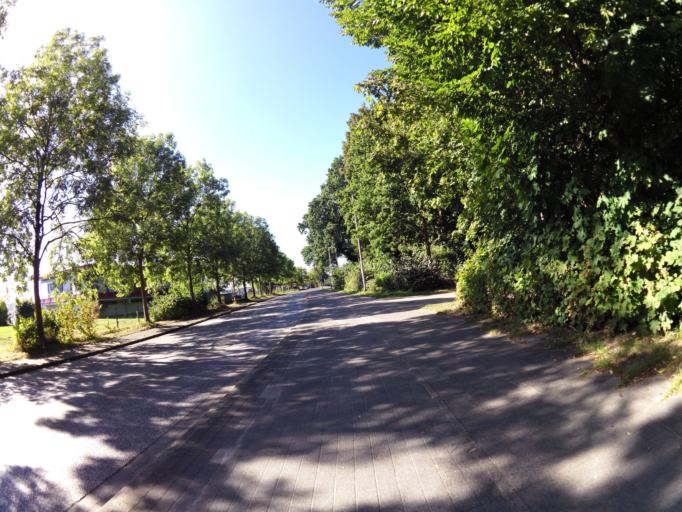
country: DE
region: Schleswig-Holstein
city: Eckernforde
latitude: 54.4772
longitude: 9.8541
